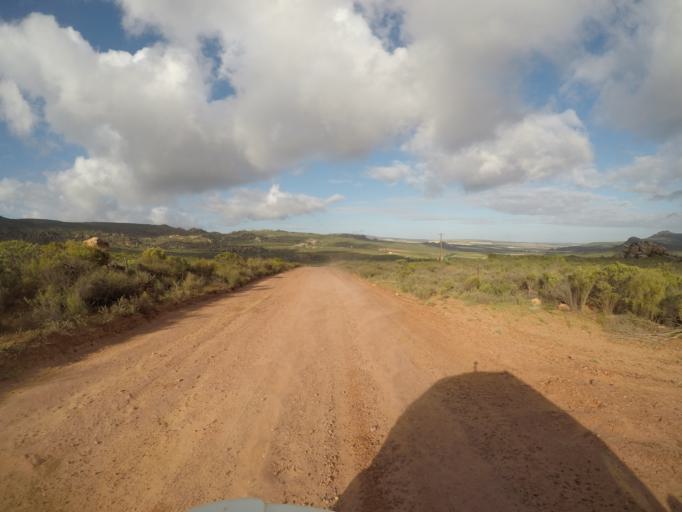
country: ZA
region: Western Cape
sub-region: West Coast District Municipality
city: Clanwilliam
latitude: -32.3432
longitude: 18.7576
